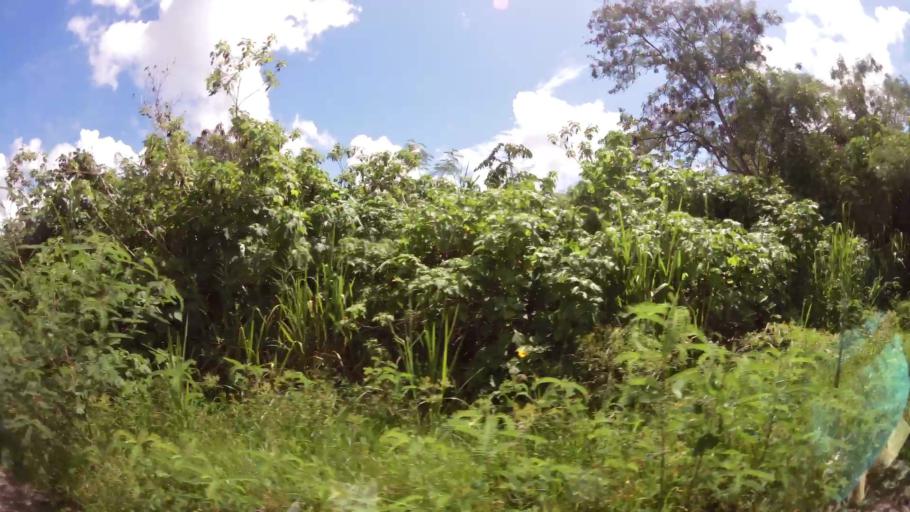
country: SR
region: Paramaribo
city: Paramaribo
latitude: 5.8623
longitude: -55.1326
